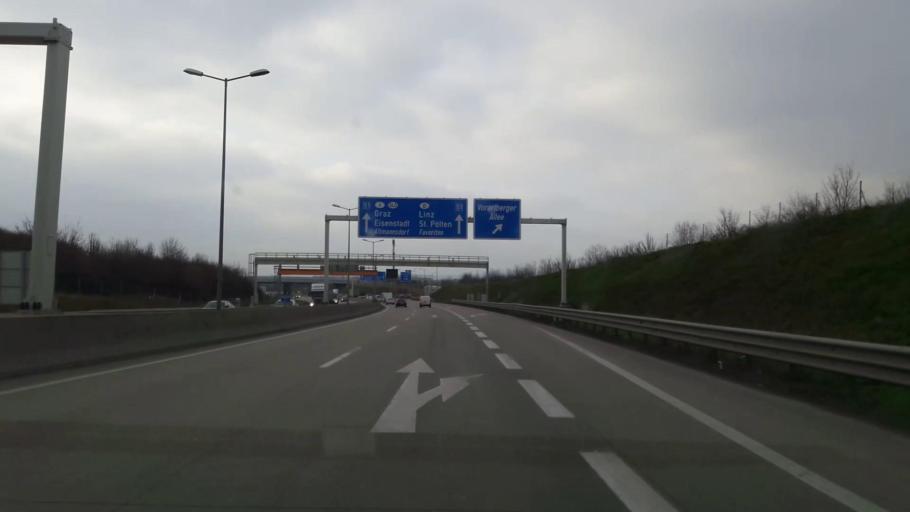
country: AT
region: Lower Austria
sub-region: Politischer Bezirk Modling
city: Vosendorf
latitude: 48.1320
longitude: 16.3460
